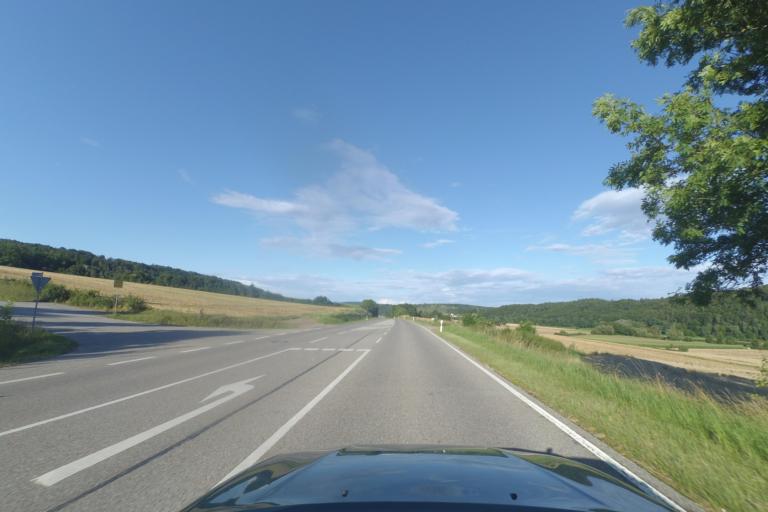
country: DE
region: Bavaria
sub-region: Upper Bavaria
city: Eichstaett
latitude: 48.8831
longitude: 11.2410
